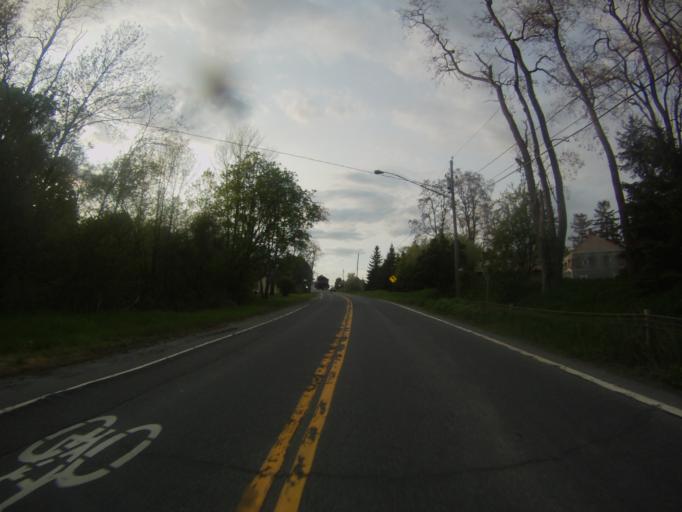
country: US
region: New York
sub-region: Essex County
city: Ticonderoga
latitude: 43.9486
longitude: -73.4180
